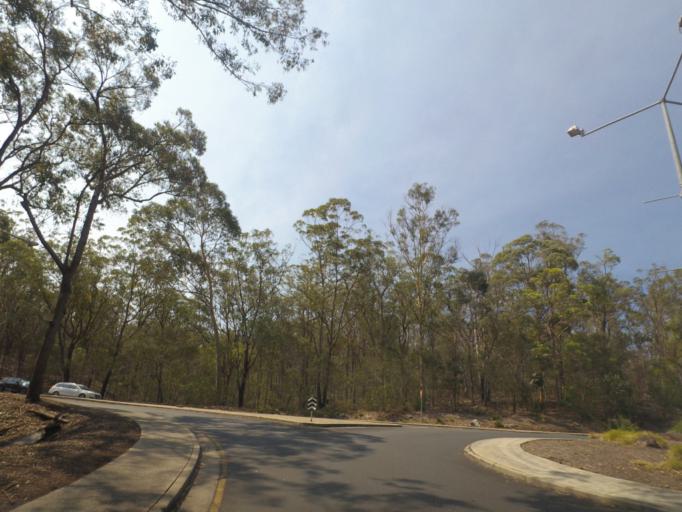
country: AU
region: Queensland
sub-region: Brisbane
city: Nathan
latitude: -27.5509
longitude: 153.0576
